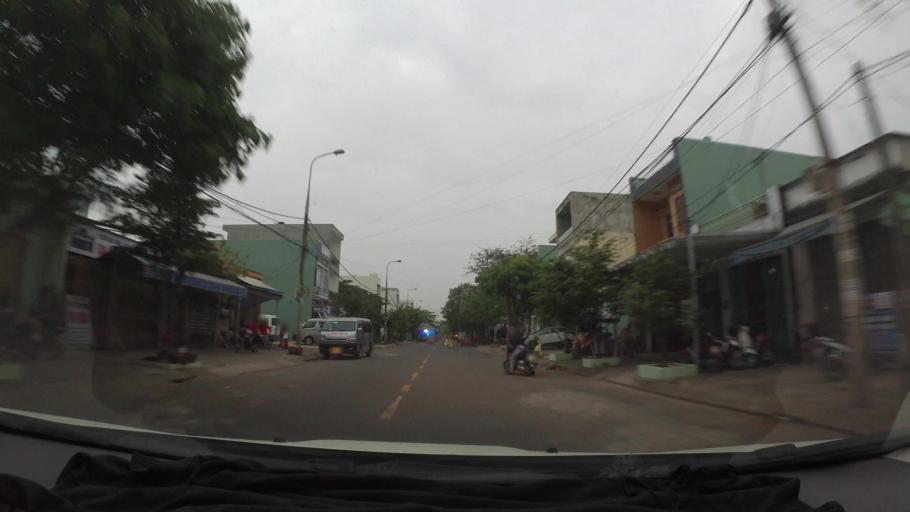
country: VN
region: Da Nang
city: Lien Chieu
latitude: 16.0539
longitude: 108.1718
